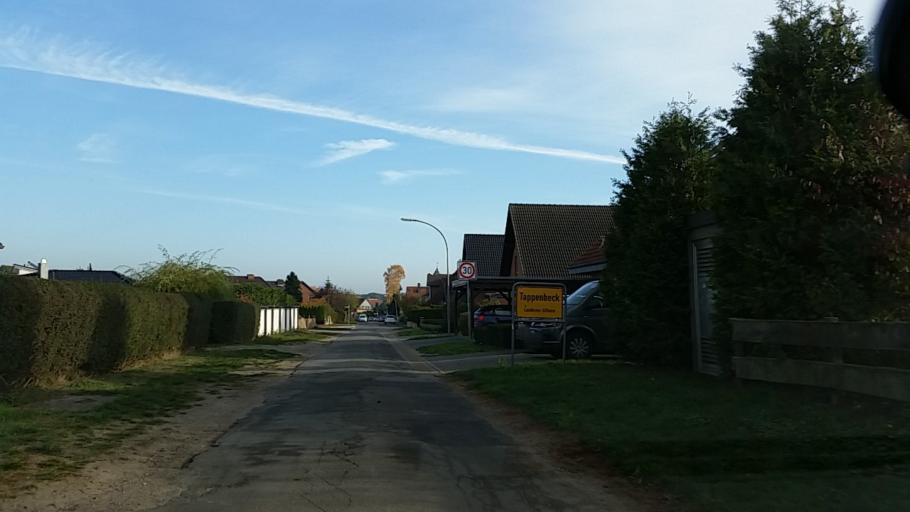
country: DE
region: Lower Saxony
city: Tappenbeck
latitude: 52.4747
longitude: 10.7396
